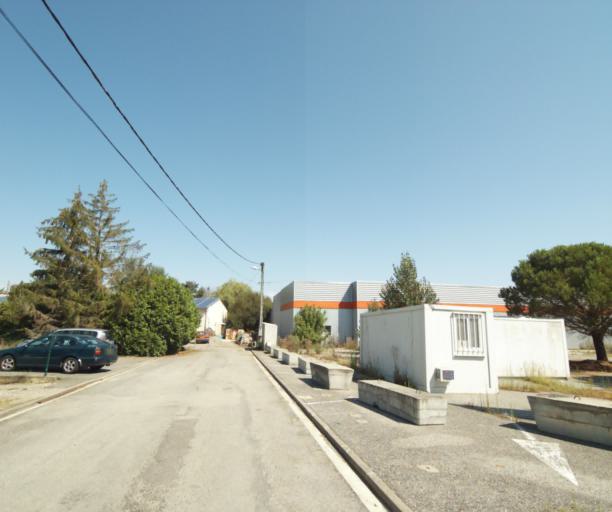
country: FR
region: Midi-Pyrenees
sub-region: Departement de l'Ariege
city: Lezat-sur-Leze
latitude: 43.2819
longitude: 1.3483
